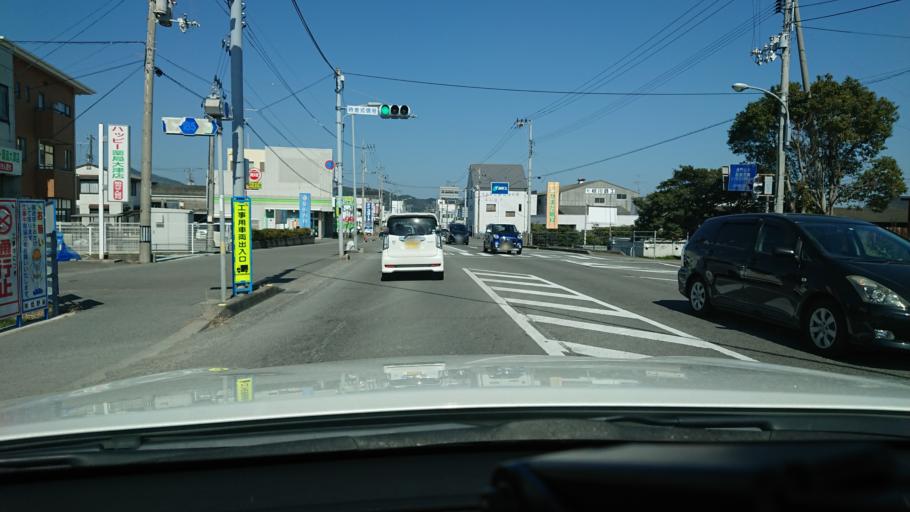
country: JP
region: Tokushima
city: Narutocho-mitsuishi
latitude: 34.1519
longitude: 134.5931
